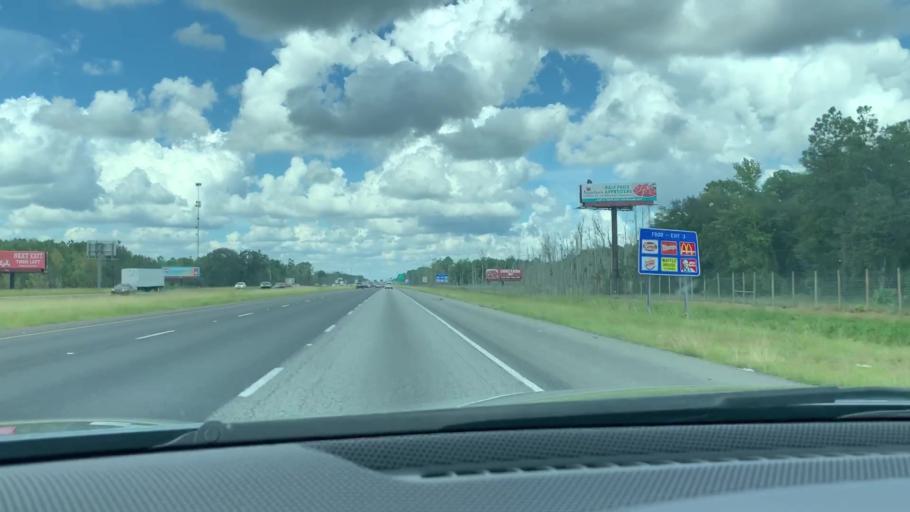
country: US
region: Georgia
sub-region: Camden County
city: Kingsland
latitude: 30.7694
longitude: -81.6542
